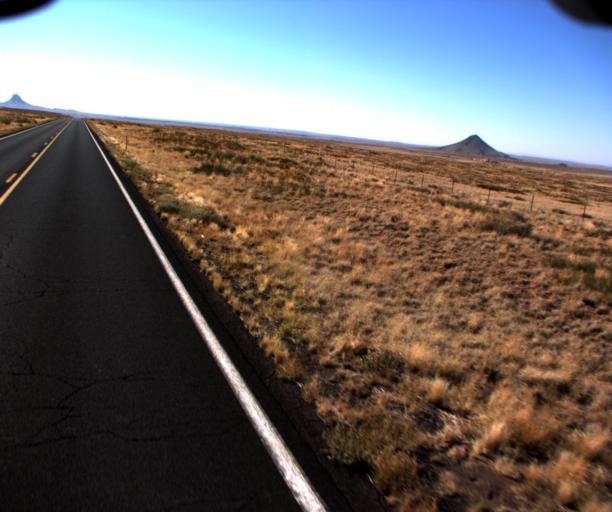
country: US
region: Arizona
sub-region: Navajo County
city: Dilkon
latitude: 35.4146
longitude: -110.4267
